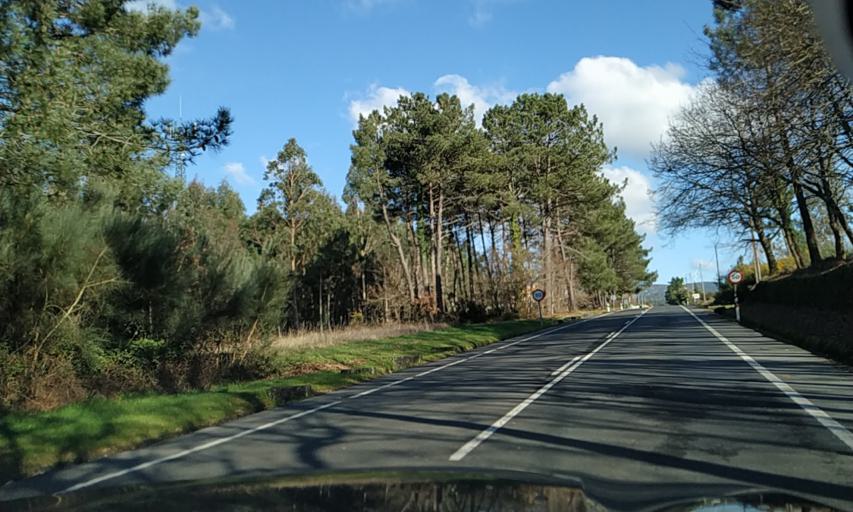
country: ES
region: Galicia
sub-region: Provincia da Coruna
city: Ribeira
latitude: 42.7067
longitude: -8.4125
